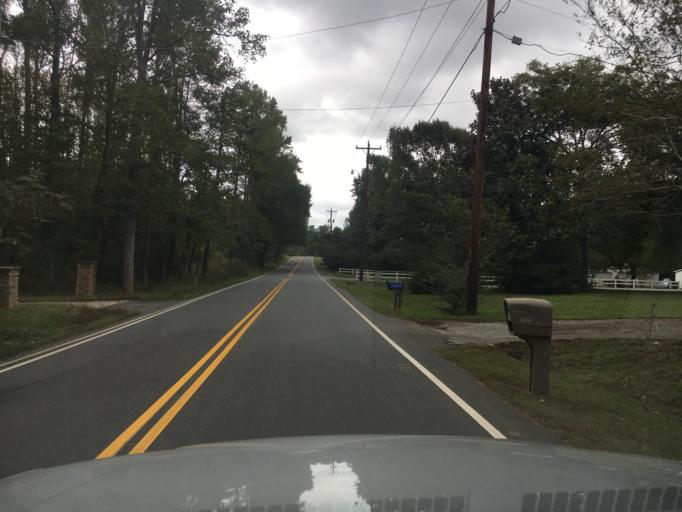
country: US
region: South Carolina
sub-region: Spartanburg County
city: Duncan
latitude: 34.8651
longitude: -82.1145
